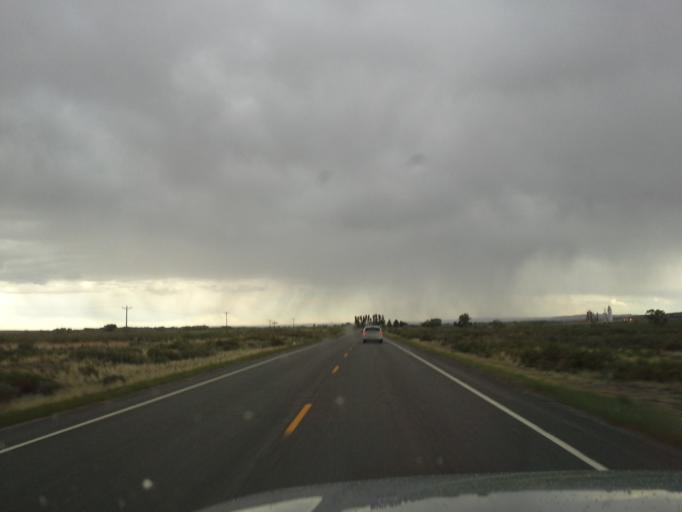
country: US
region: Wyoming
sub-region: Park County
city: Powell
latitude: 45.0109
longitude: -108.6255
